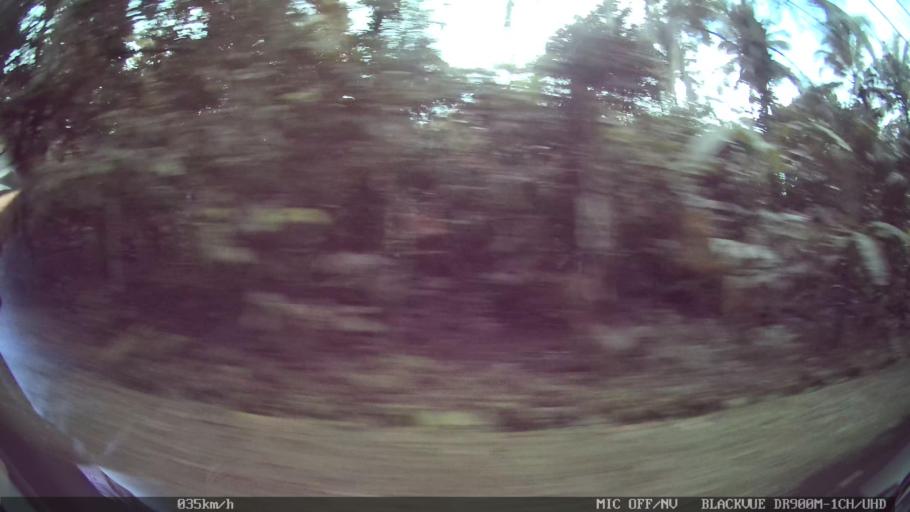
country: ID
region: Bali
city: Petang
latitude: -8.4121
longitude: 115.2239
